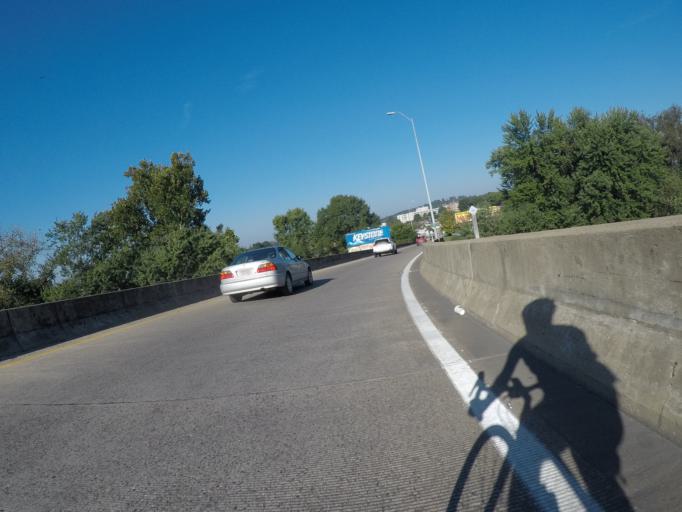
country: US
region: West Virginia
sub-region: Cabell County
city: Huntington
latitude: 38.4287
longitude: -82.3917
